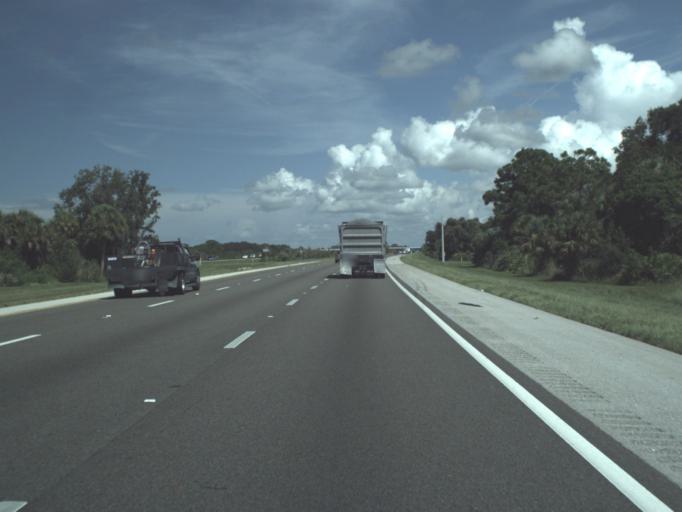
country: US
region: Florida
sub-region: Sarasota County
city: Laurel
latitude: 27.1765
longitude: -82.4348
